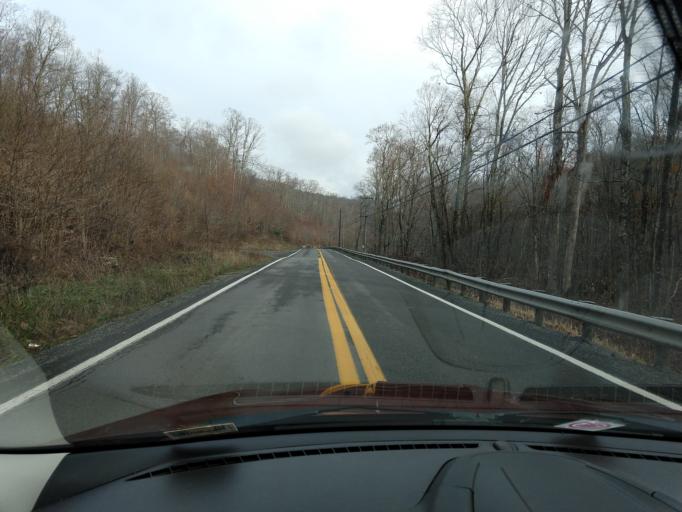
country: US
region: West Virginia
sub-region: Greenbrier County
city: Rainelle
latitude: 38.0860
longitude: -80.7078
